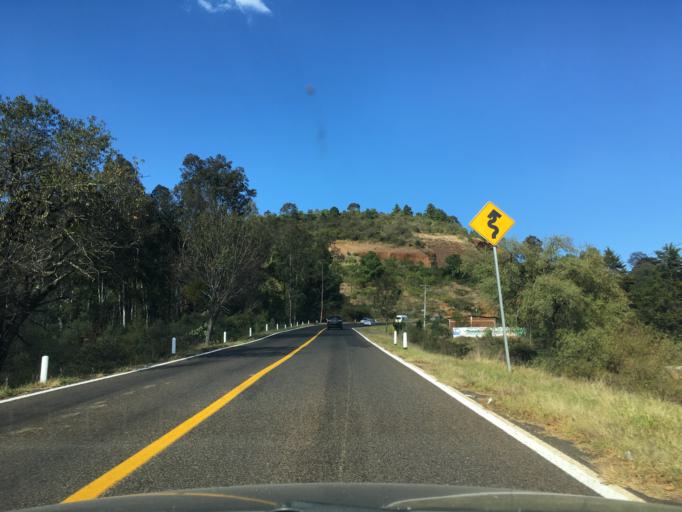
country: MX
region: Michoacan
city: Tzintzuntzan
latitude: 19.5970
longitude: -101.5784
